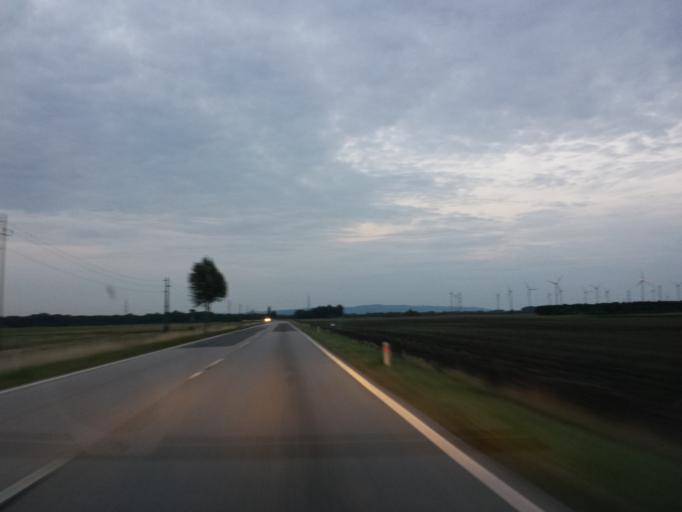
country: AT
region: Lower Austria
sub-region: Politischer Bezirk Baden
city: Oberwaltersdorf
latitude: 47.9682
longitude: 16.3392
